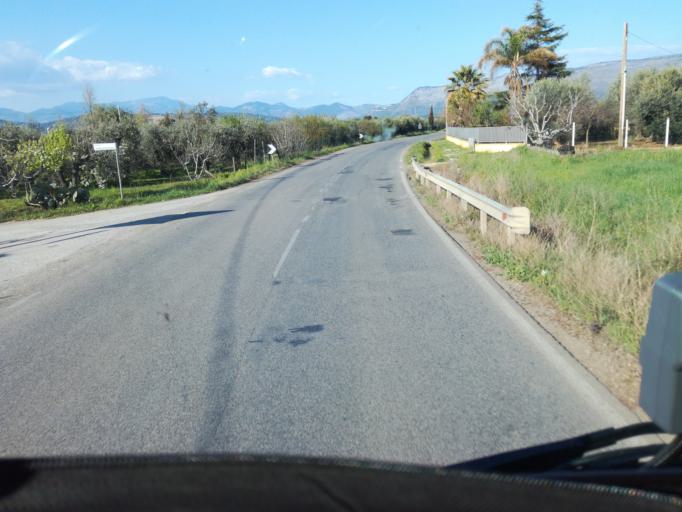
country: IT
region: Latium
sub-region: Provincia di Latina
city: Priverno
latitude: 41.3985
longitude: 13.1574
